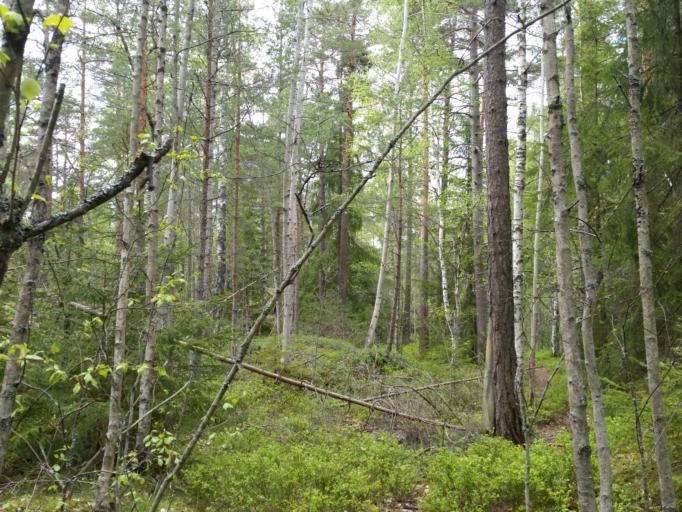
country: SE
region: Stockholm
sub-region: Sollentuna Kommun
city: Sollentuna
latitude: 59.4654
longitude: 17.9523
